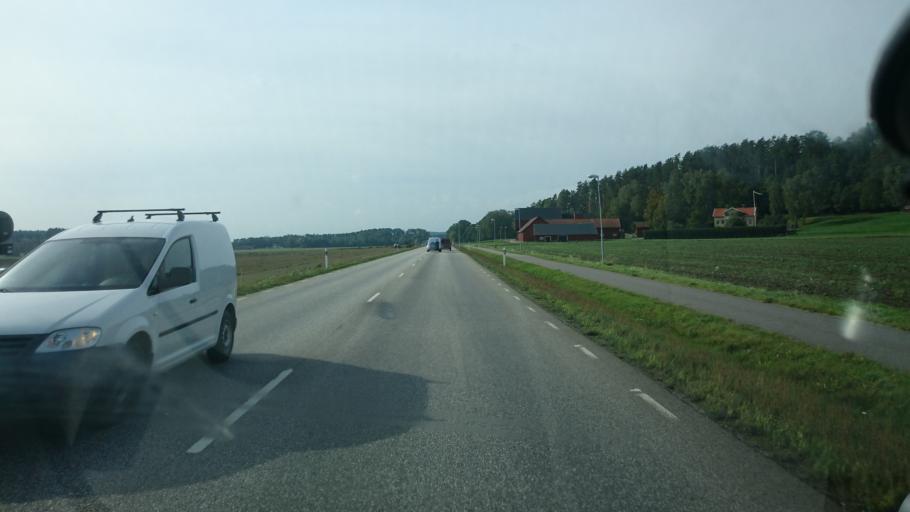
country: SE
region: Vaestra Goetaland
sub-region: Alingsas Kommun
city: Sollebrunn
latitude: 58.1130
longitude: 12.5279
